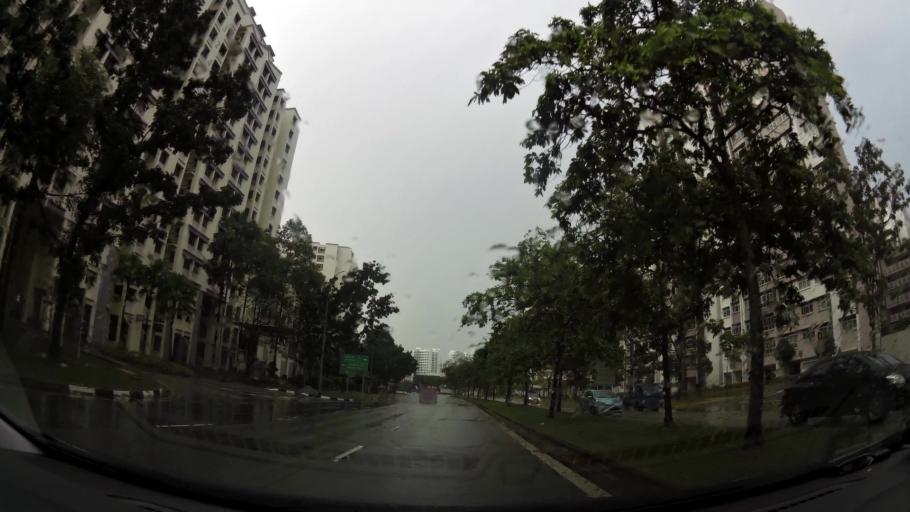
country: MY
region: Johor
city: Kampung Pasir Gudang Baru
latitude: 1.3938
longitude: 103.8924
